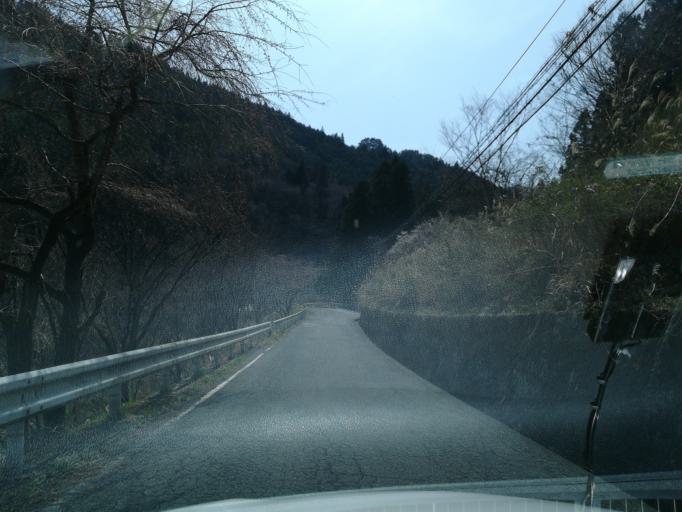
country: JP
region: Tokushima
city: Ikedacho
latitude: 33.8641
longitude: 133.9563
